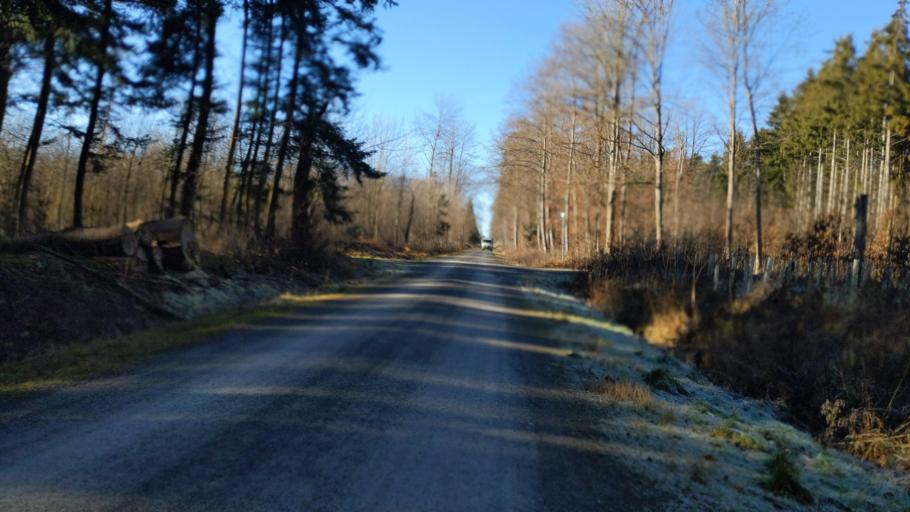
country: DE
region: Baden-Wuerttemberg
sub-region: Regierungsbezirk Stuttgart
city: Renningen
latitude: 48.7885
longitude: 8.9255
